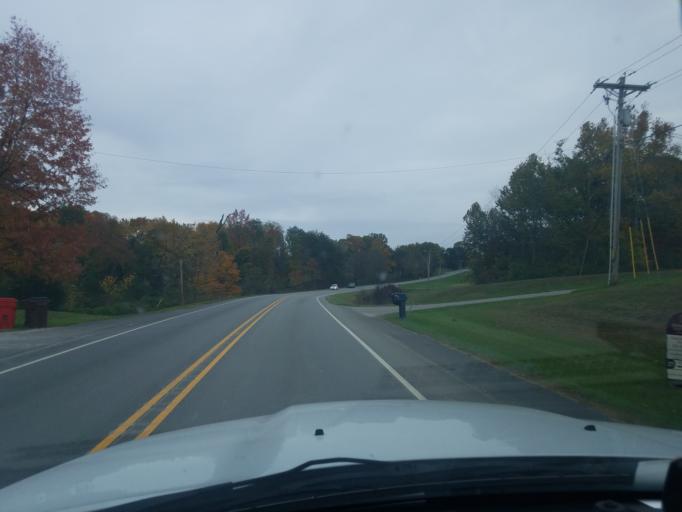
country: US
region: Indiana
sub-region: Clark County
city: Sellersburg
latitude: 38.4434
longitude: -85.8264
